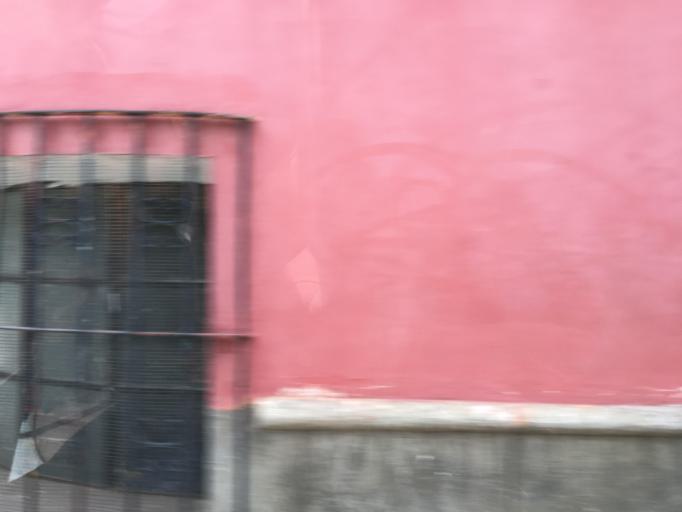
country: GT
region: Sacatepequez
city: Jocotenango
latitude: 14.5727
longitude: -90.7402
